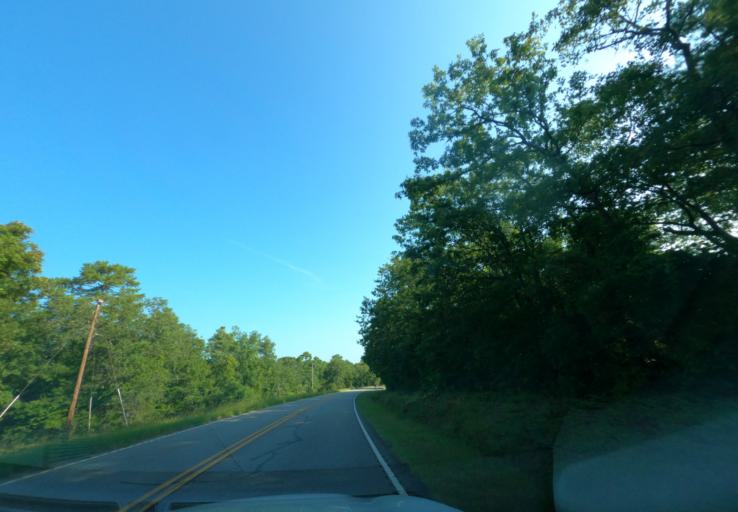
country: US
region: South Carolina
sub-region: Edgefield County
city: Murphys Estates
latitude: 33.5877
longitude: -81.9791
